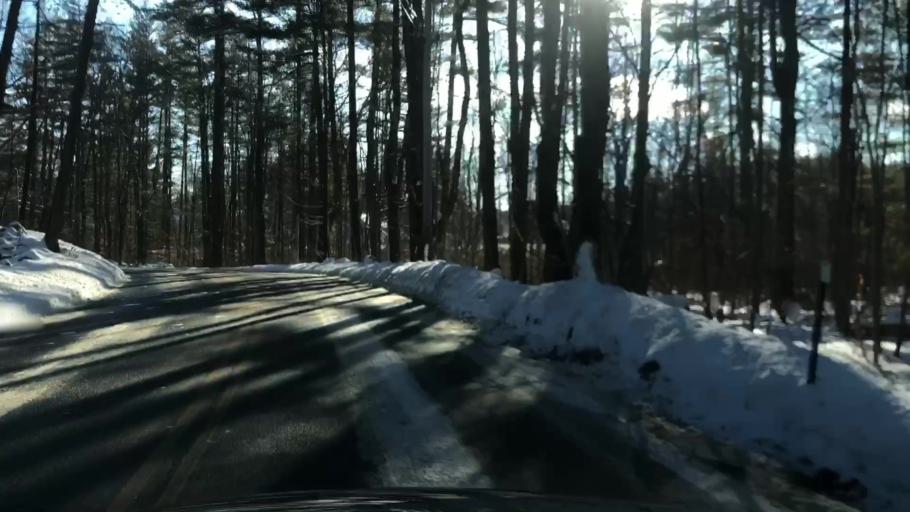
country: US
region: New Hampshire
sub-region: Hillsborough County
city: Wilton
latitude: 42.8247
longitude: -71.7150
